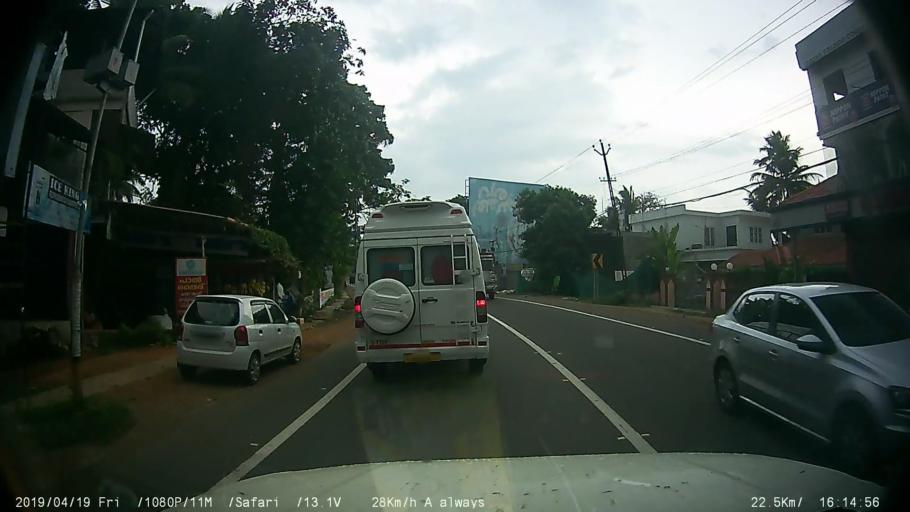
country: IN
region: Kerala
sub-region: Kottayam
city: Kottayam
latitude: 9.6324
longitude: 76.5428
